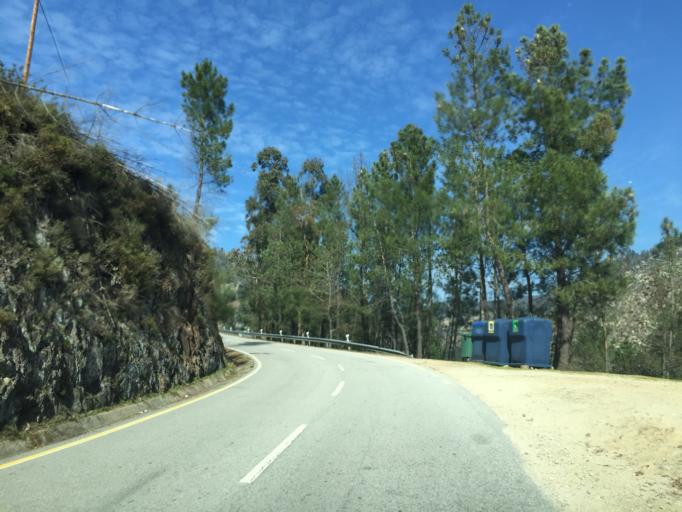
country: PT
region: Aveiro
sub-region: Arouca
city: Arouca
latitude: 40.9538
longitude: -8.1741
